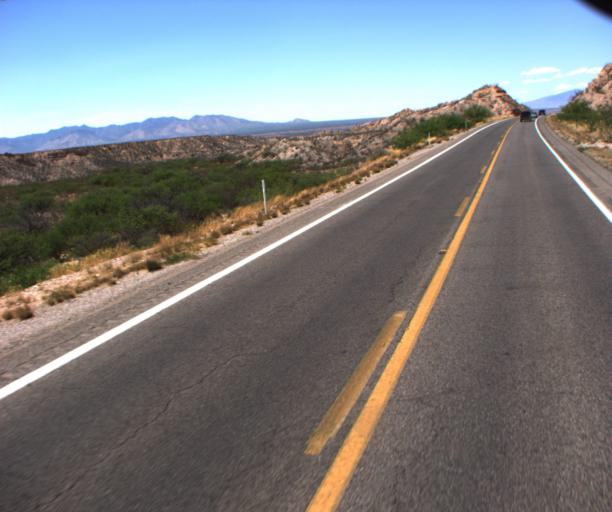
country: US
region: Arizona
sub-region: Cochise County
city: Saint David
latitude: 31.8198
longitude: -110.1710
